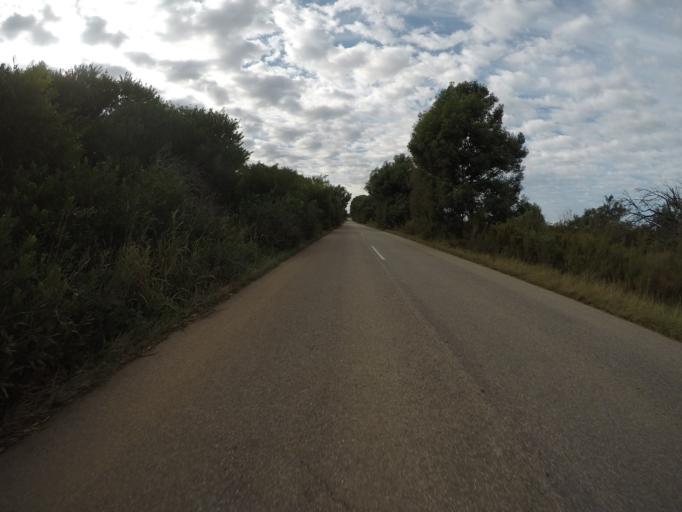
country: ZA
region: Eastern Cape
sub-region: Cacadu District Municipality
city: Kareedouw
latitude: -34.0447
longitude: 24.4394
